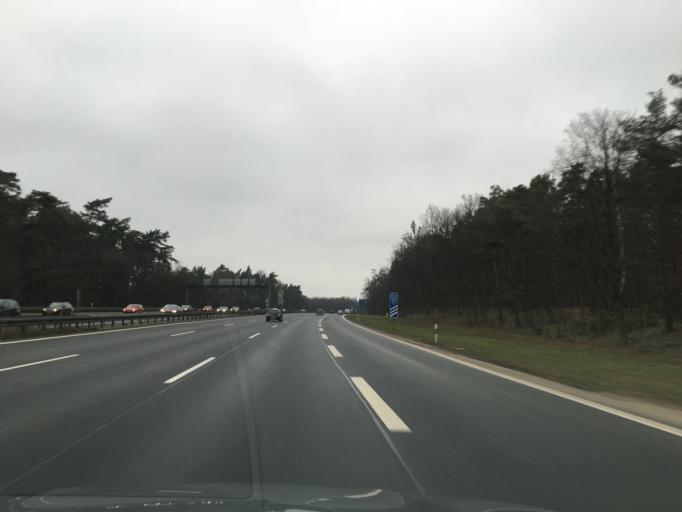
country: DE
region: Bavaria
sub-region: Regierungsbezirk Mittelfranken
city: Feucht
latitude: 49.4020
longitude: 11.1968
